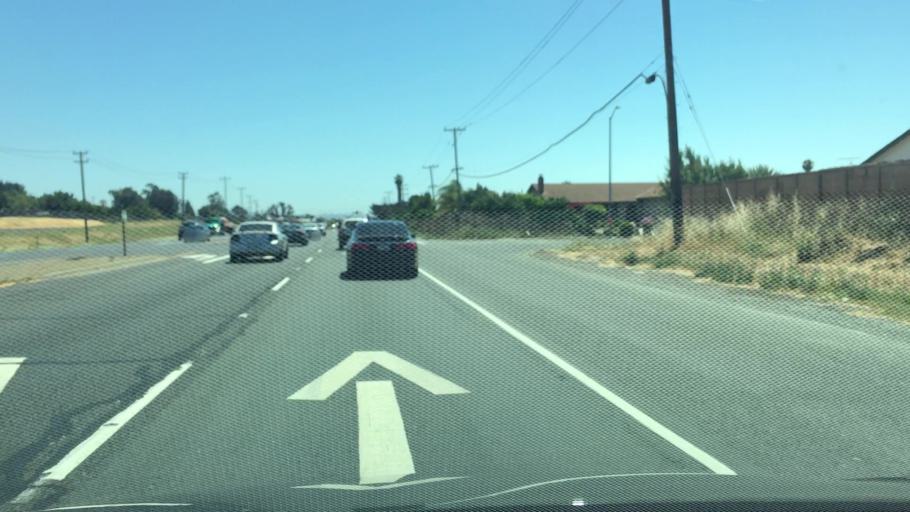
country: US
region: California
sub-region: Napa County
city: American Canyon
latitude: 38.1593
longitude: -122.2534
